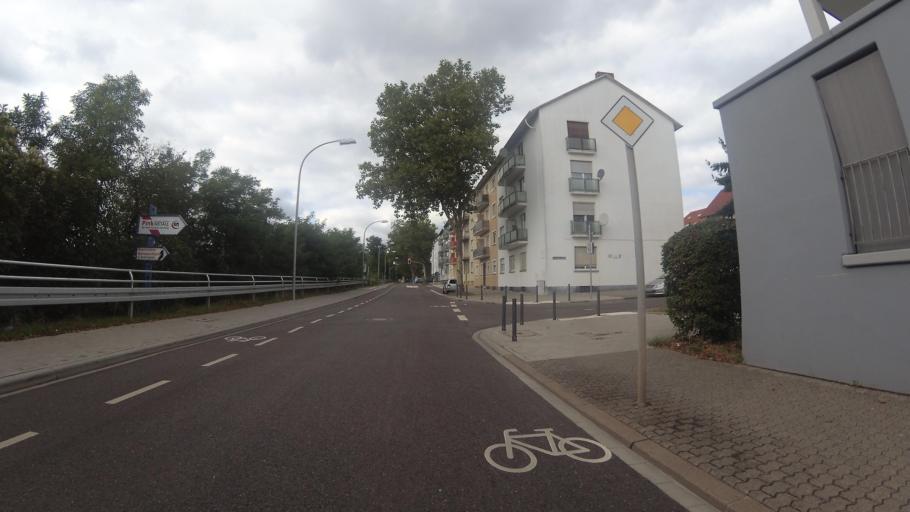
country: DE
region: Saarland
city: Saarbrucken
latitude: 49.2428
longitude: 6.9579
